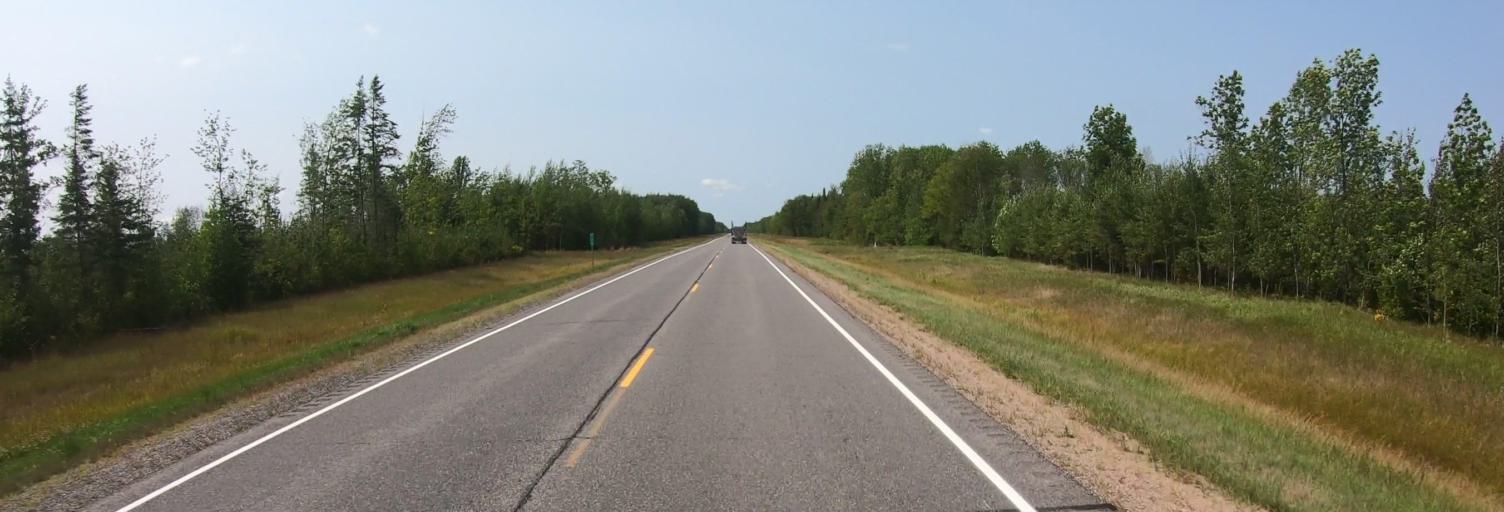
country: US
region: Minnesota
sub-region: Koochiching County
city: International Falls
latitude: 48.5127
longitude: -93.7431
